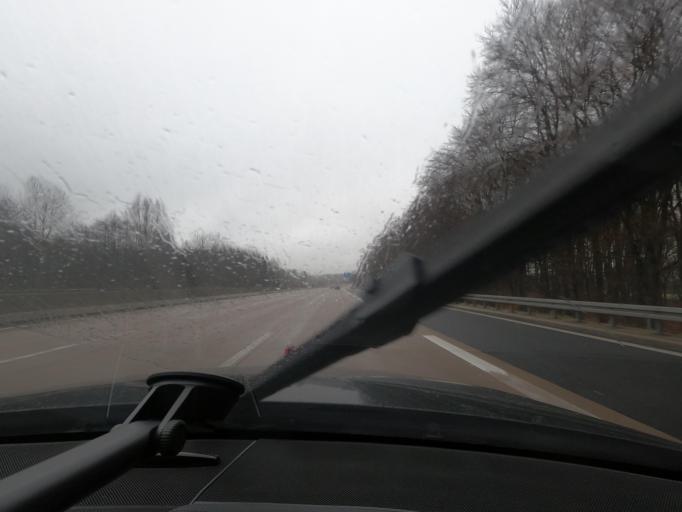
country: DE
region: Lower Saxony
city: Garlstorf
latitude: 53.2287
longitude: 10.0765
